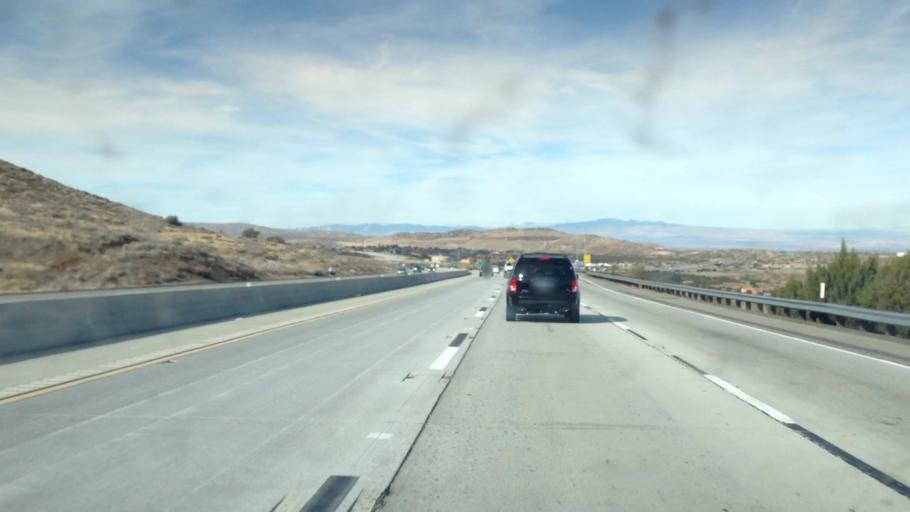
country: US
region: California
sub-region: Los Angeles County
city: Vincent
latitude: 34.5394
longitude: -118.1215
